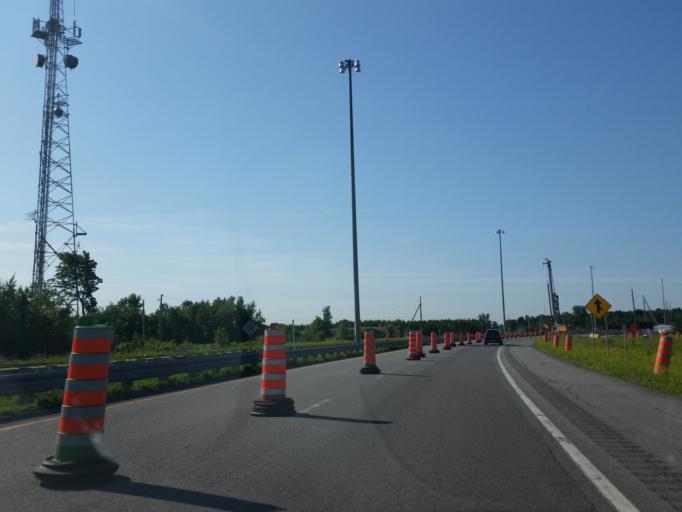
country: CA
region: Quebec
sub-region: Monteregie
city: Napierville
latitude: 45.2686
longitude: -73.4682
